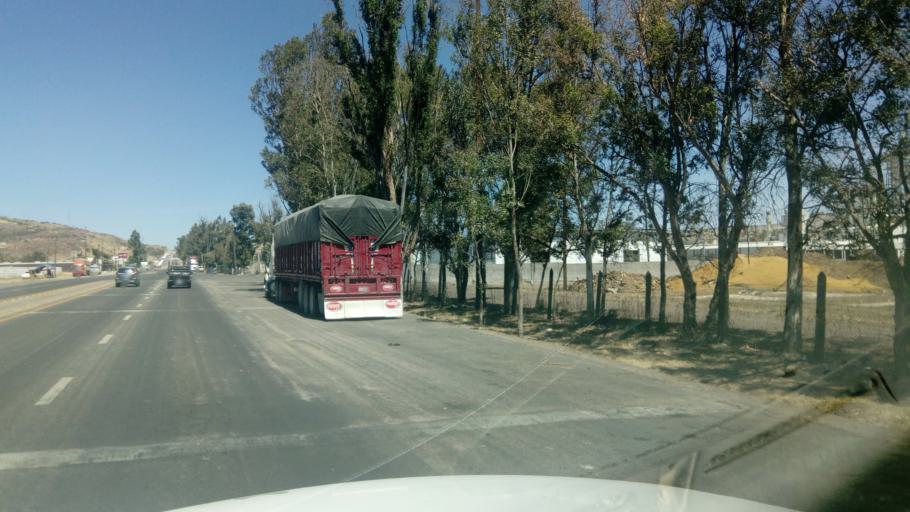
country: MX
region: Durango
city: Victoria de Durango
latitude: 24.0774
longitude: -104.6651
